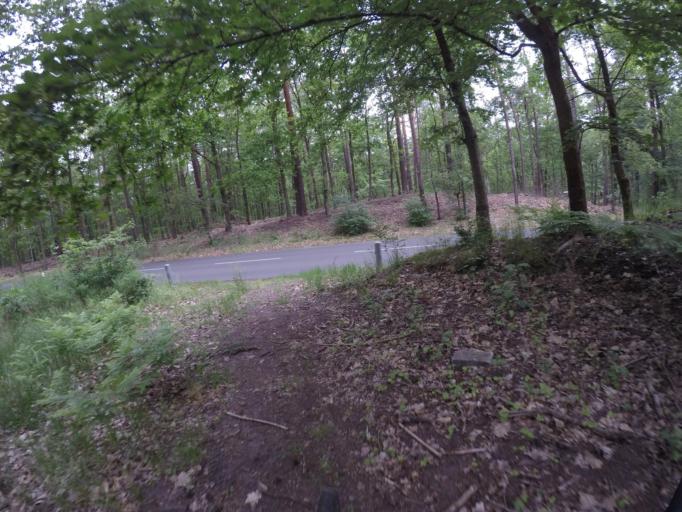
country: DE
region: Berlin
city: Heiligensee
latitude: 52.6256
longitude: 13.2549
